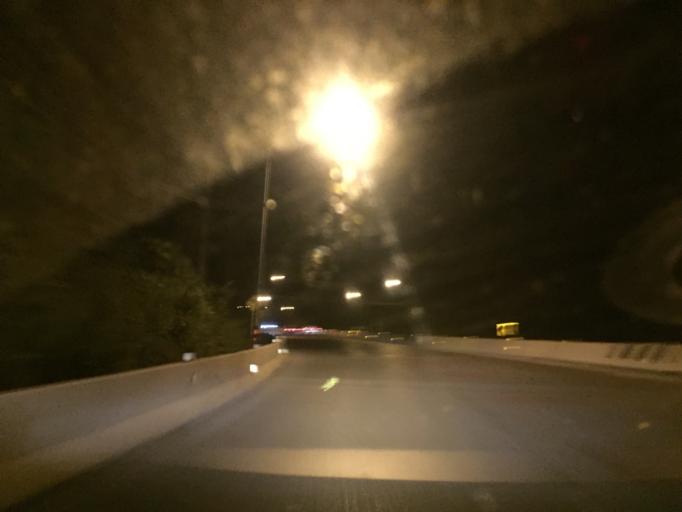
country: TH
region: Changwat Nong Bua Lamphu
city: Nong Bua Lamphu
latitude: 17.2383
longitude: 102.5058
